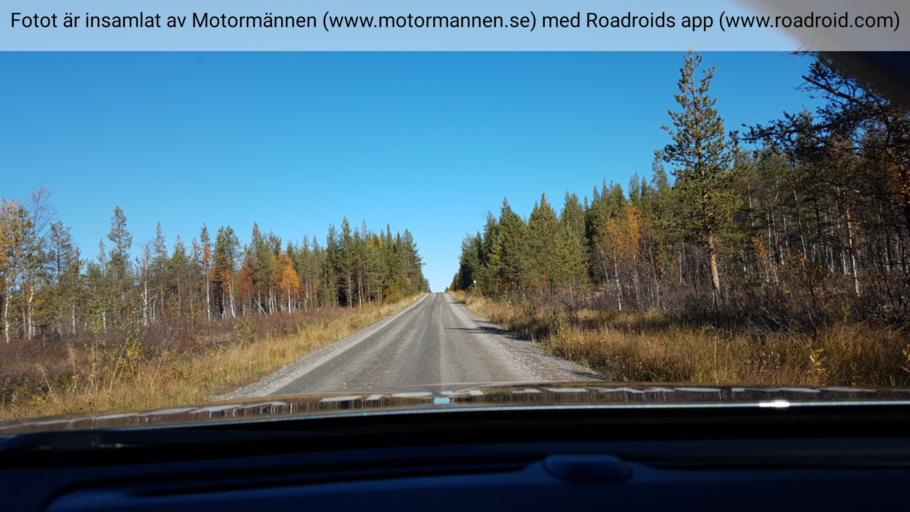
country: SE
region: Norrbotten
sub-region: Gallivare Kommun
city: Gaellivare
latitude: 66.5724
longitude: 21.0716
